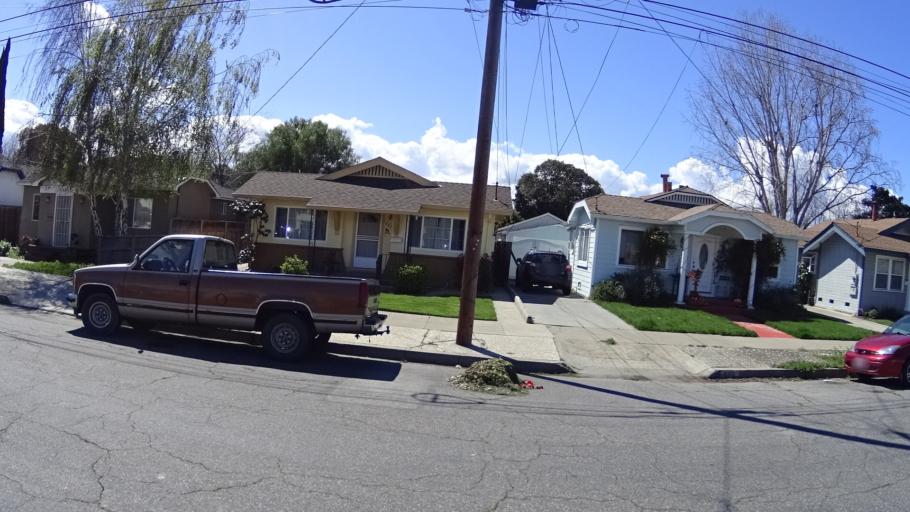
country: US
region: California
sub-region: Santa Clara County
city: San Jose
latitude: 37.3545
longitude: -121.8848
